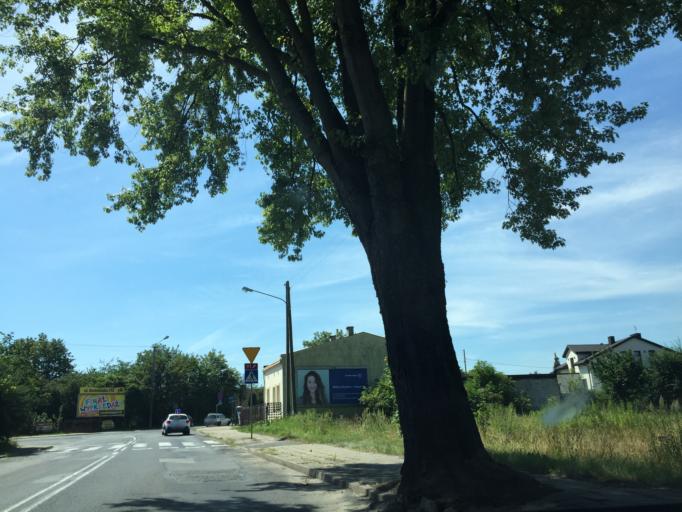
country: PL
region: Lodz Voivodeship
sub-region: Piotrkow Trybunalski
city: Piotrkow Trybunalski
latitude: 51.4160
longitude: 19.7123
